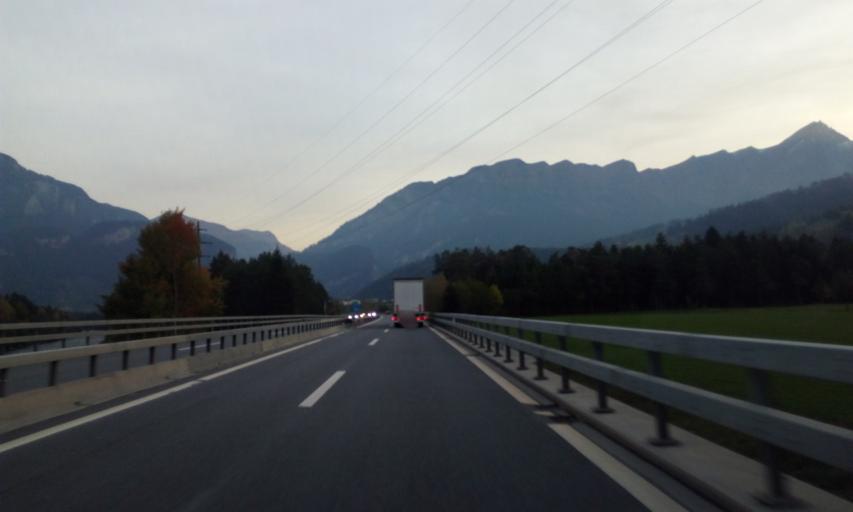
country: CH
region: Grisons
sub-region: Hinterrhein District
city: Cazis
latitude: 46.7264
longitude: 9.4401
